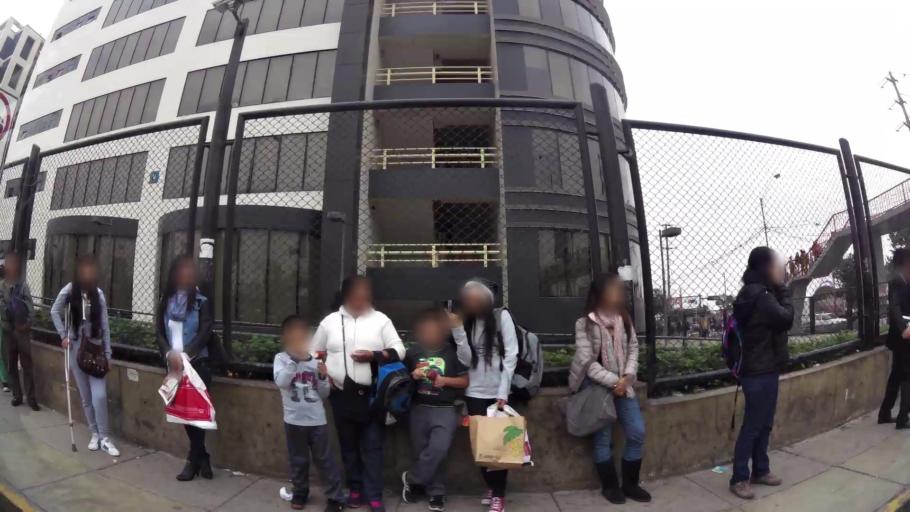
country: PE
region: Lima
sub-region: Lima
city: San Luis
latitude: -12.0841
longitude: -76.9729
